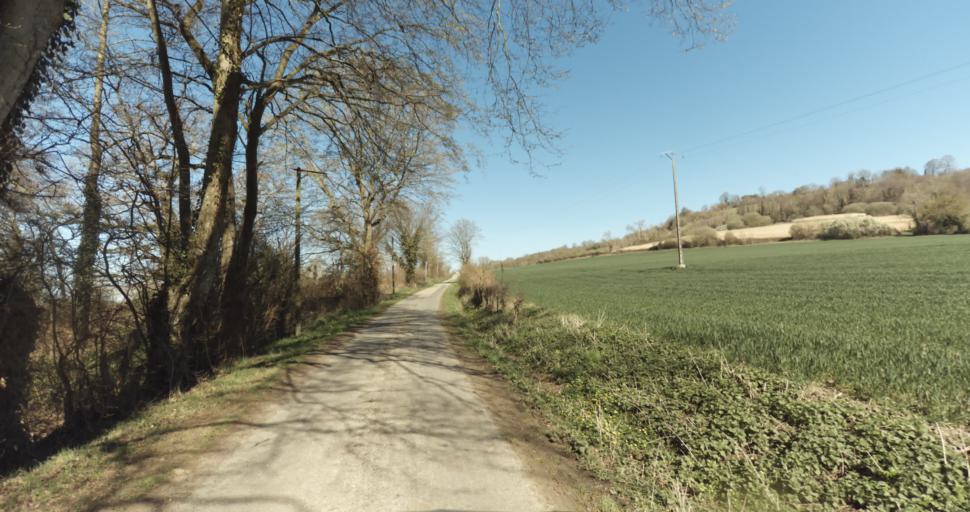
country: FR
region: Lower Normandy
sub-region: Departement du Calvados
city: Livarot
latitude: 48.9607
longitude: 0.0683
